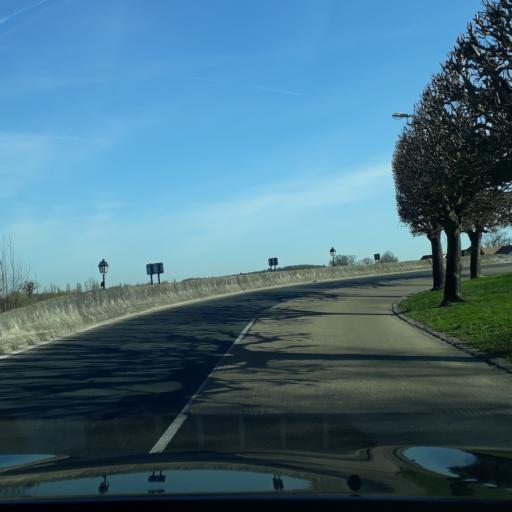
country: FR
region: Ile-de-France
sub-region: Departement de l'Essonne
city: Baulne
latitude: 48.4941
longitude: 2.3618
